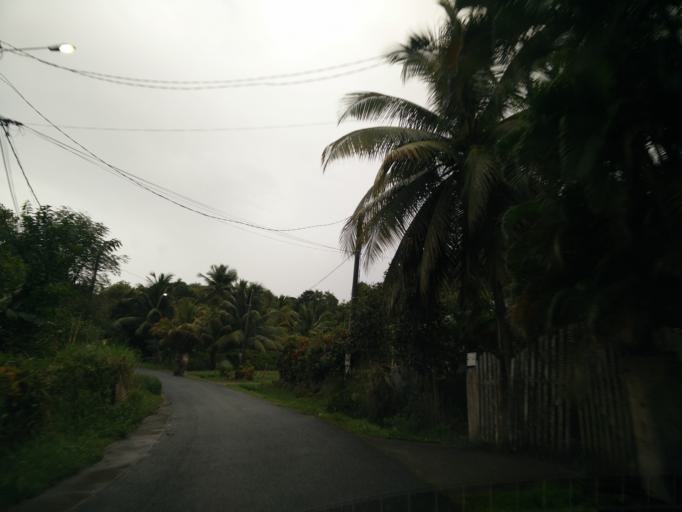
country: GP
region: Guadeloupe
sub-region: Guadeloupe
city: Le Gosier
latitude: 16.2363
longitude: -61.4890
